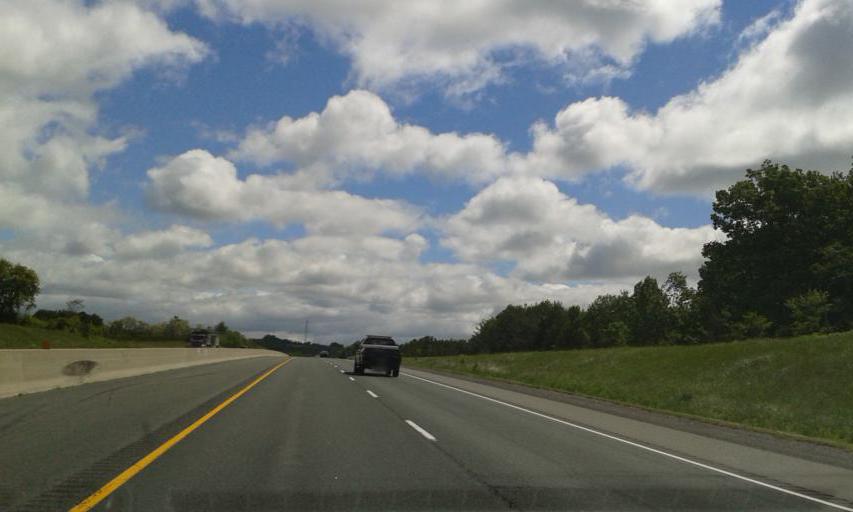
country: CA
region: Ontario
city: Quinte West
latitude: 44.0558
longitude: -77.8164
